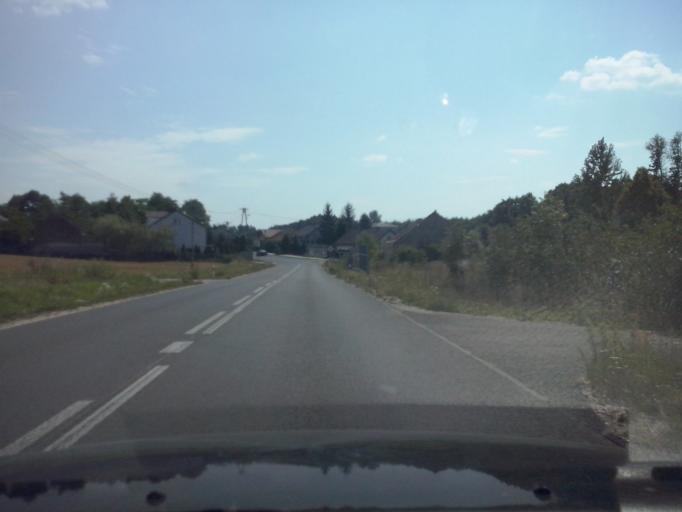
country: PL
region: Swietokrzyskie
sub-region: Powiat kielecki
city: Chmielnik
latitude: 50.6101
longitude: 20.7946
